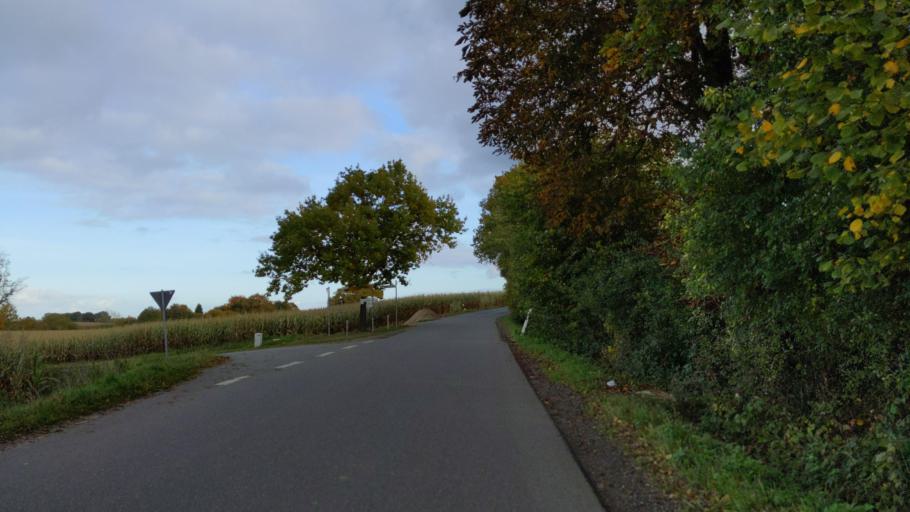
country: DE
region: Schleswig-Holstein
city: Susel
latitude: 54.1036
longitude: 10.7209
